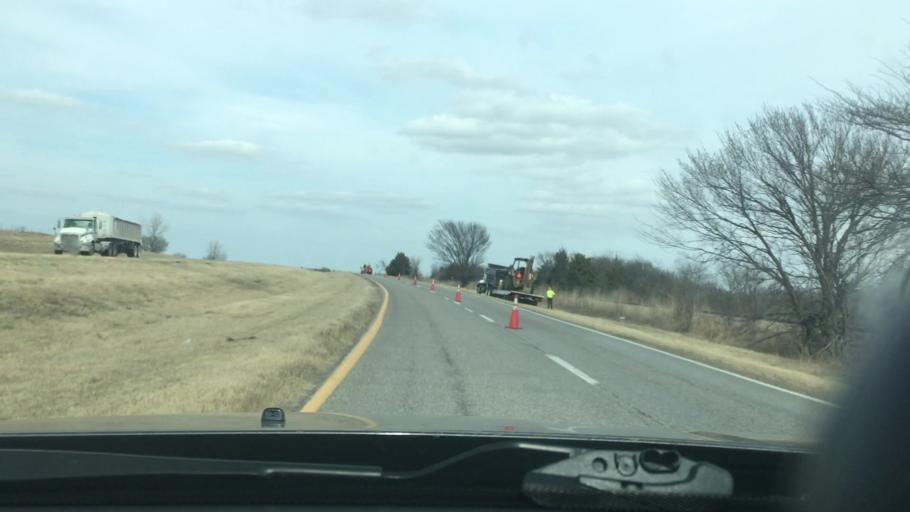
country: US
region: Oklahoma
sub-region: Pontotoc County
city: Ada
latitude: 34.7044
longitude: -96.7316
